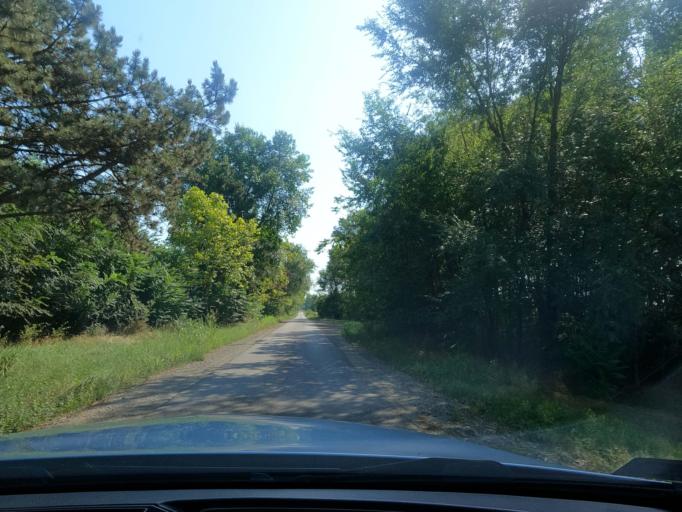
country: RS
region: Autonomna Pokrajina Vojvodina
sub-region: Juznobacki Okrug
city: Becej
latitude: 45.6639
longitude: 19.9078
